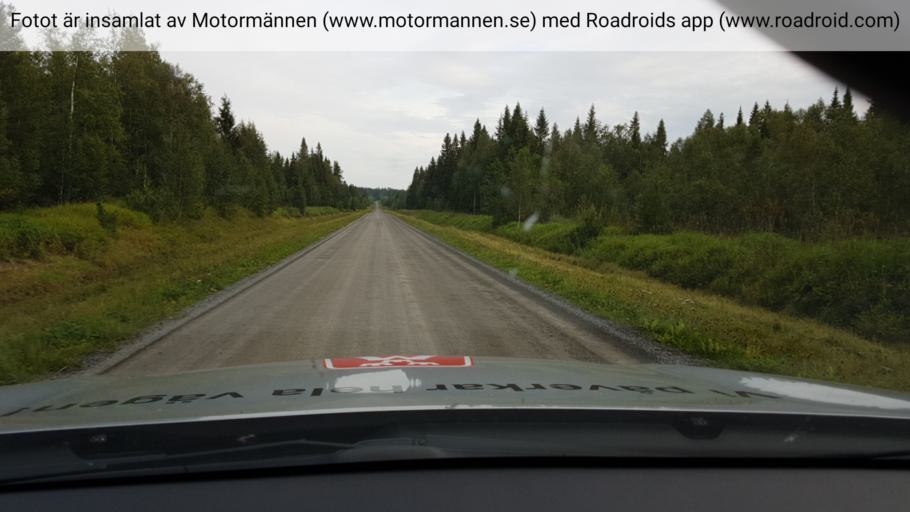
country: SE
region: Jaemtland
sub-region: OEstersunds Kommun
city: Lit
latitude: 63.6555
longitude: 14.9272
